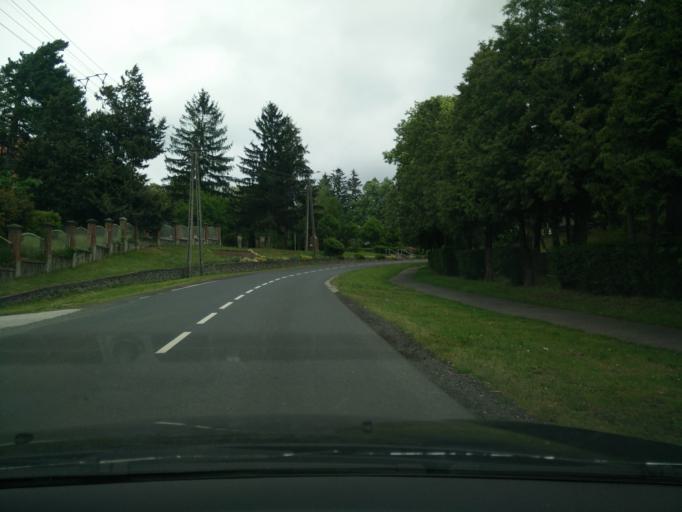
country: HU
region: Zala
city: Turje
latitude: 46.9848
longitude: 17.1038
